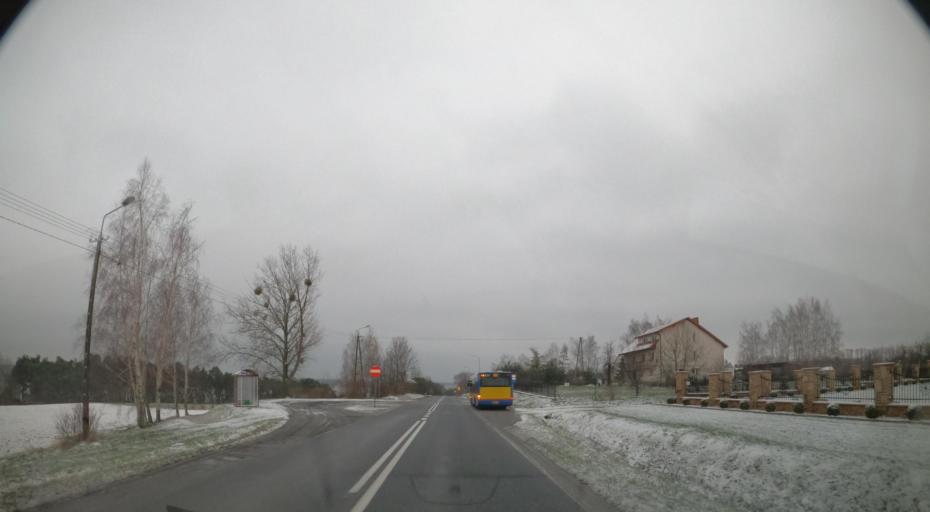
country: PL
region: Masovian Voivodeship
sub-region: Powiat plocki
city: Maszewo Duze
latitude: 52.5707
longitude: 19.5759
